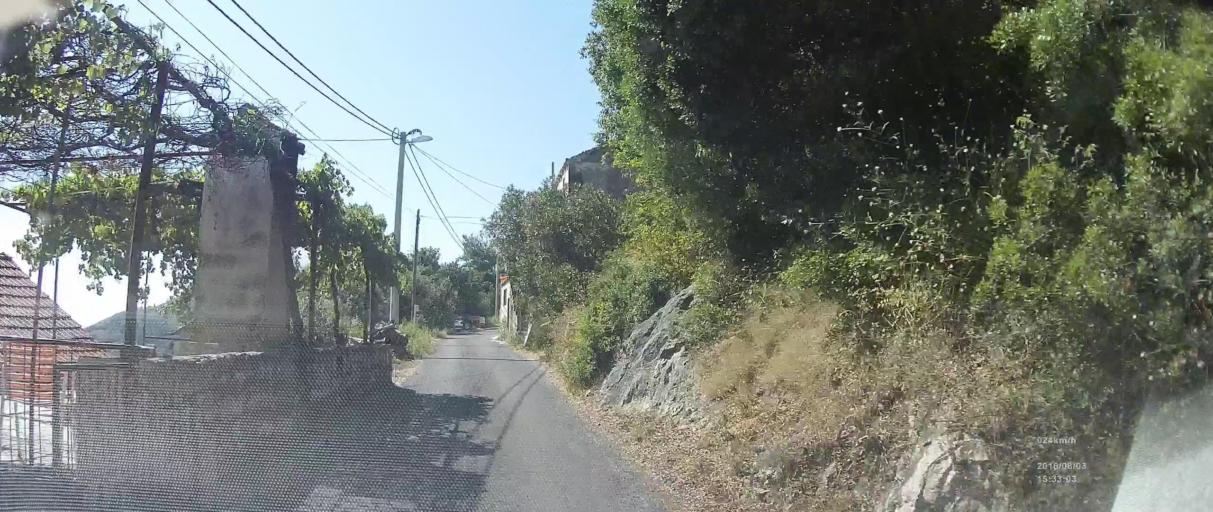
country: HR
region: Dubrovacko-Neretvanska
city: Blato
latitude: 42.7337
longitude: 17.5564
